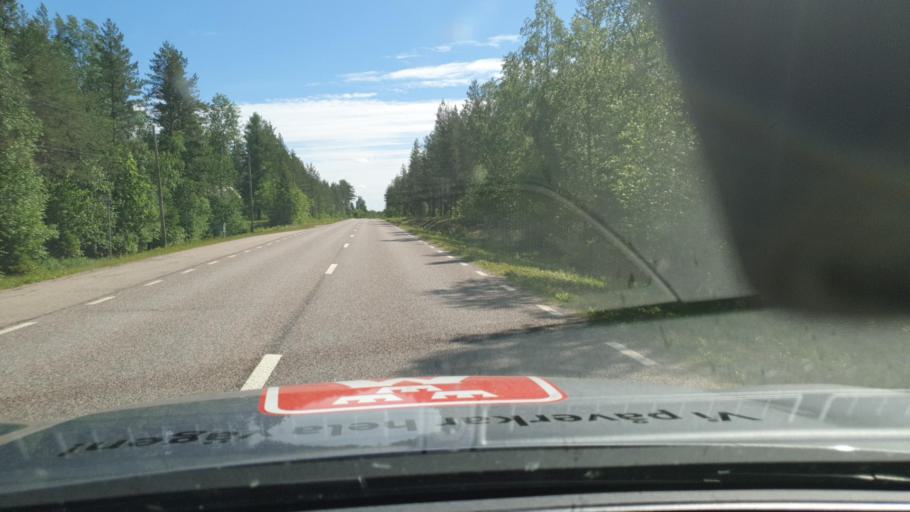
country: FI
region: Lapland
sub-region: Torniolaakso
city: Pello
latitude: 66.9731
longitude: 23.8108
